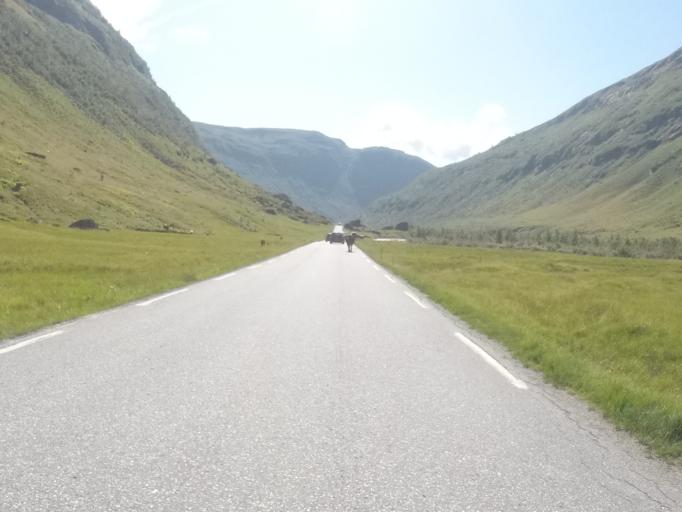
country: NO
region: Sogn og Fjordane
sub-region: Vik
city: Vik
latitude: 60.8967
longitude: 6.4913
